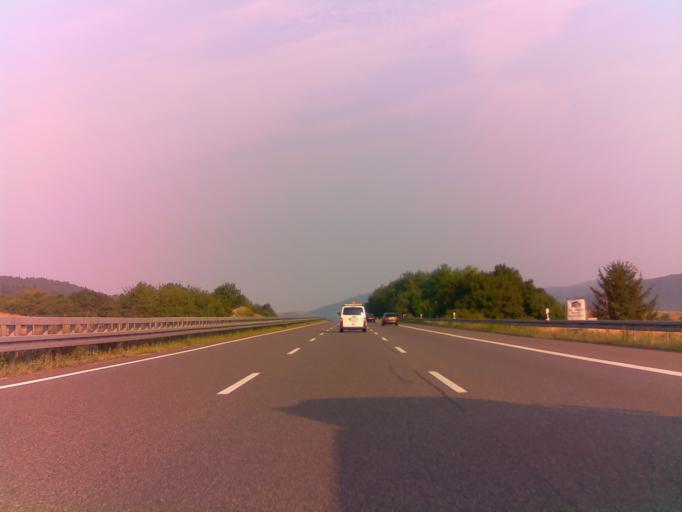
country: DE
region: Hesse
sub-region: Regierungsbezirk Kassel
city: Herleshausen
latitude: 51.0154
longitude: 10.1417
